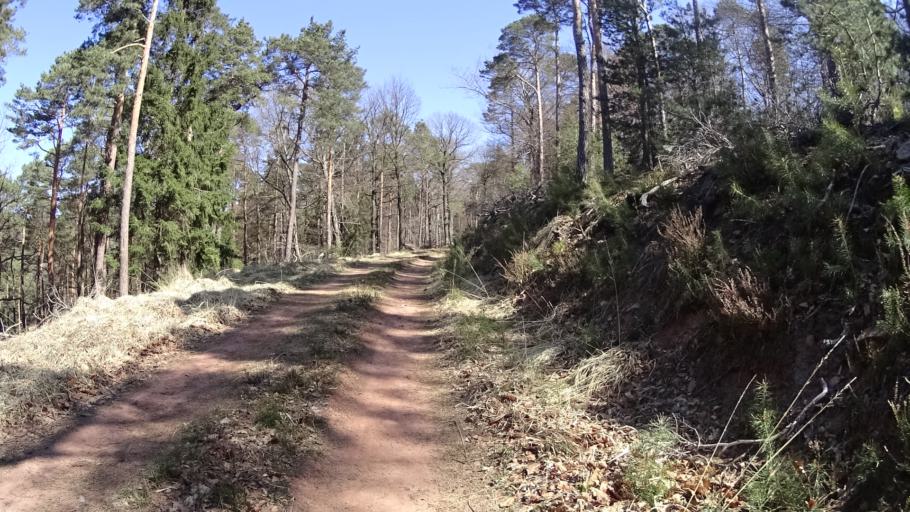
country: DE
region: Rheinland-Pfalz
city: Neidenfels
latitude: 49.3928
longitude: 8.0648
